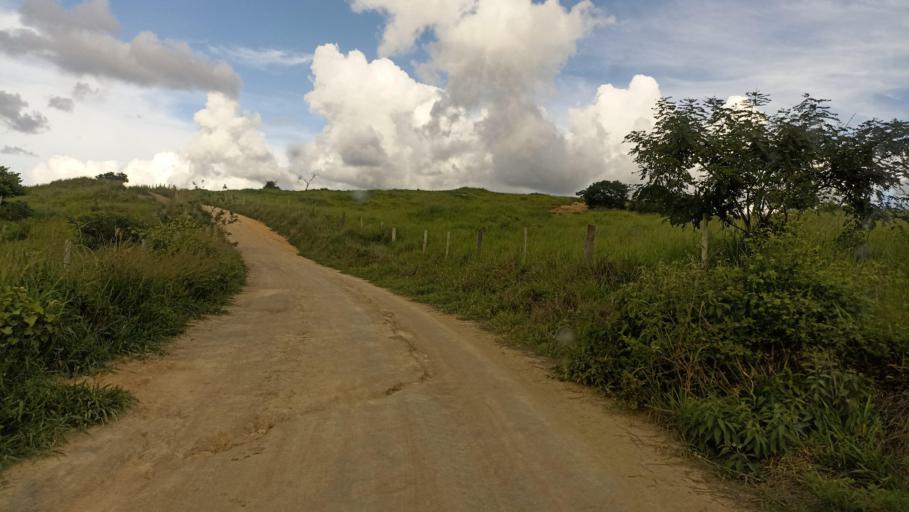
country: BR
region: Minas Gerais
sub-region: Almenara
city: Almenara
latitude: -16.5483
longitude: -40.4514
